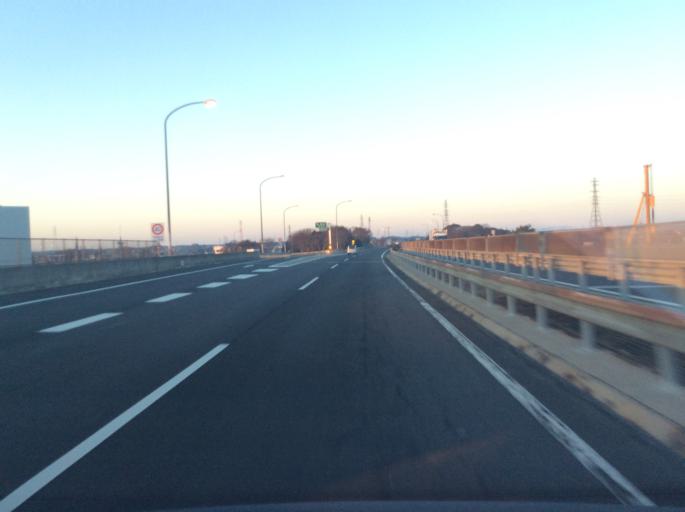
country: JP
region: Ibaraki
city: Funaishikawa
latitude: 36.5106
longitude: 140.5778
